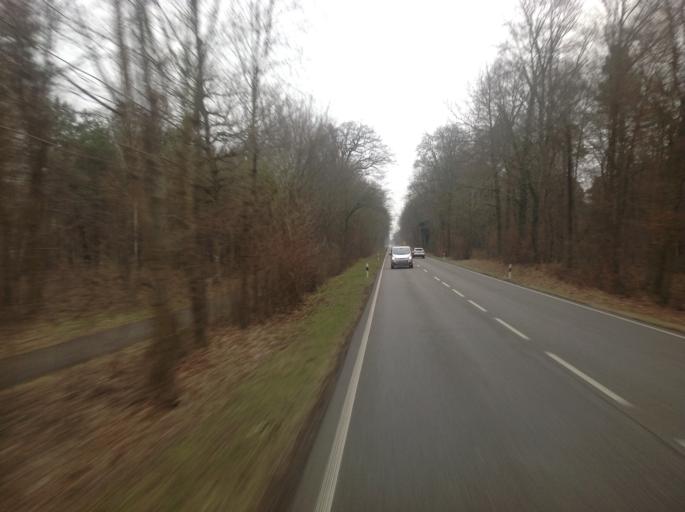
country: DE
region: Baden-Wuerttemberg
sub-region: Karlsruhe Region
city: Iffezheim
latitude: 48.8303
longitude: 8.1741
